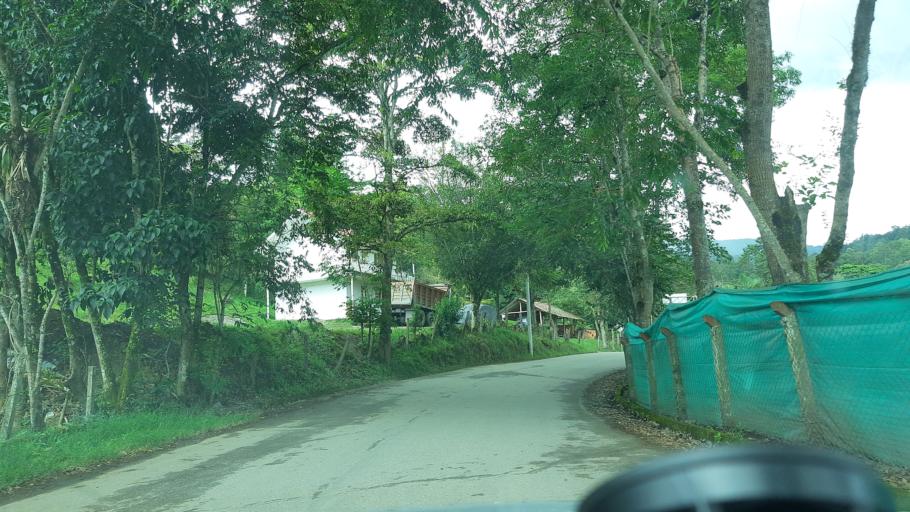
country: CO
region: Boyaca
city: Garagoa
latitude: 5.0940
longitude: -73.3648
